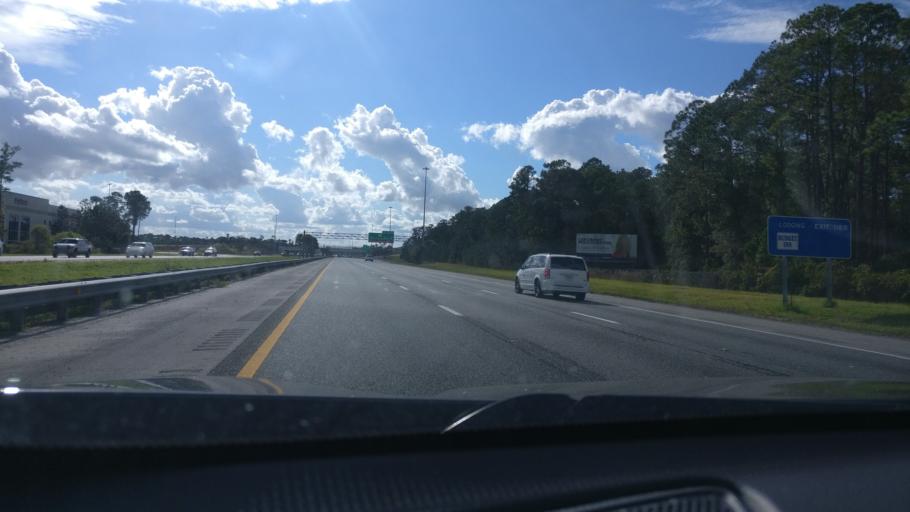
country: US
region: Florida
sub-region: Volusia County
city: Lake Helen
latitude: 29.0237
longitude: -81.2266
